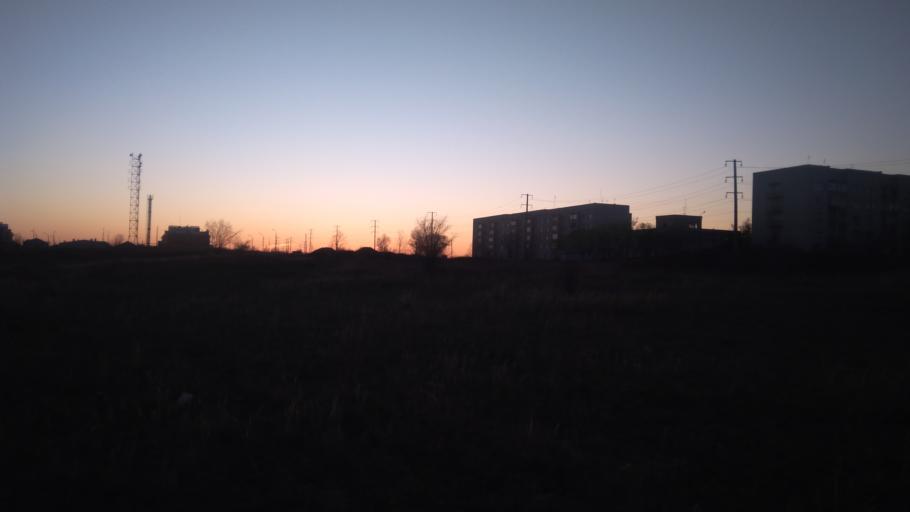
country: RU
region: Chelyabinsk
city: Troitsk
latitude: 54.0765
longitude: 61.5250
